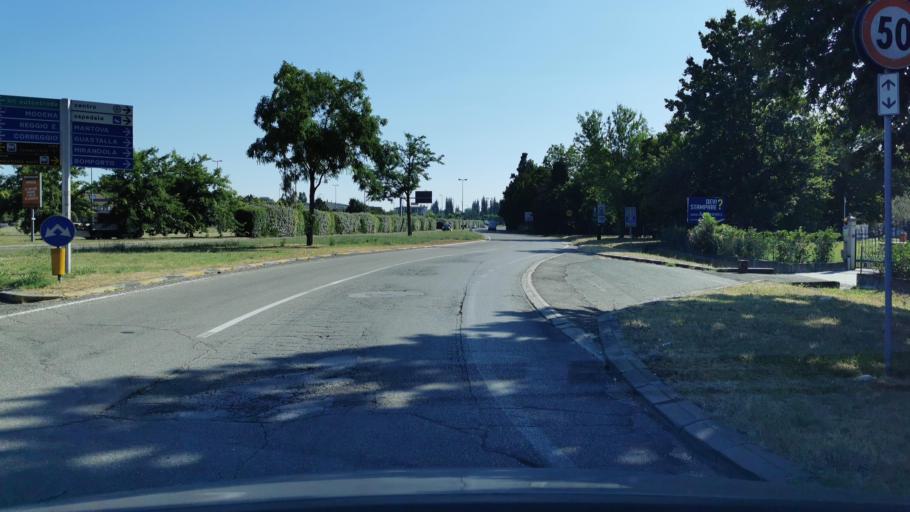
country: IT
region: Emilia-Romagna
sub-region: Provincia di Modena
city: Santa Croce Scuole
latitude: 44.7723
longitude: 10.8563
